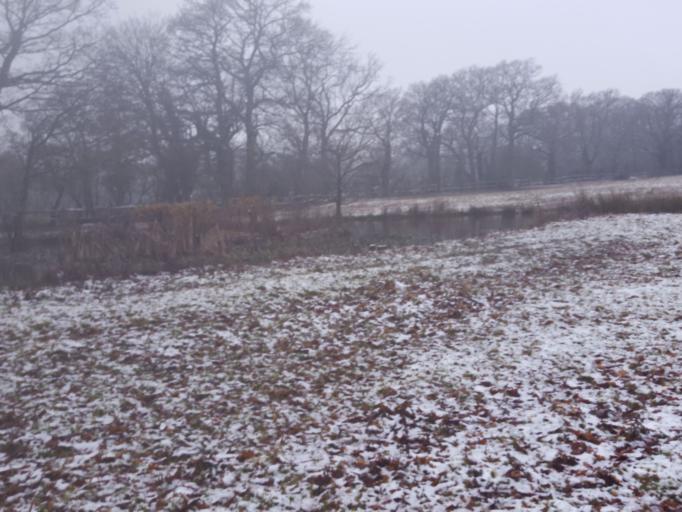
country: GB
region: England
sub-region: West Sussex
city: Gossops Green
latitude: 51.1280
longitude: -0.2293
